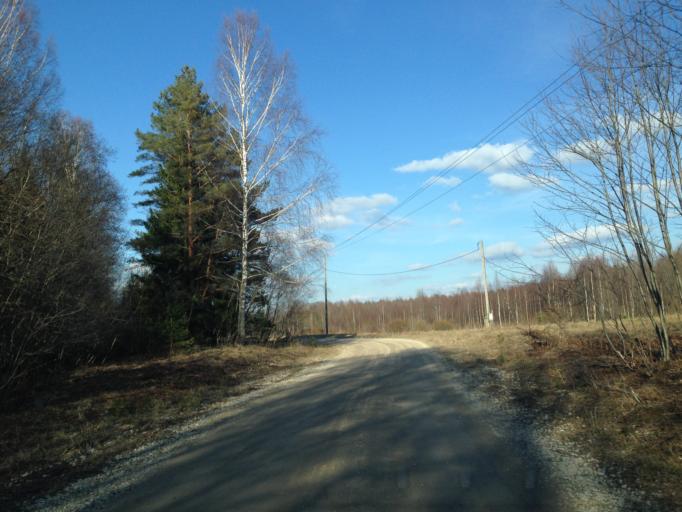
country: EE
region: Harju
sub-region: Nissi vald
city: Turba
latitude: 59.1352
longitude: 24.1722
